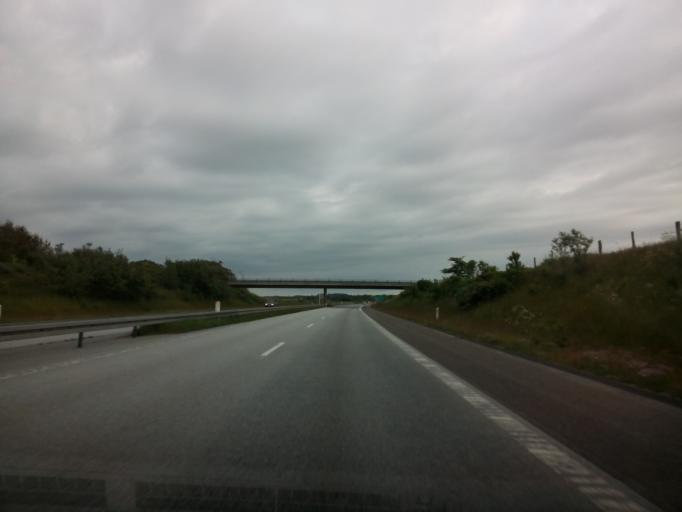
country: DK
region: North Denmark
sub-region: Hjorring Kommune
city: Vra
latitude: 57.3555
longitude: 10.0301
